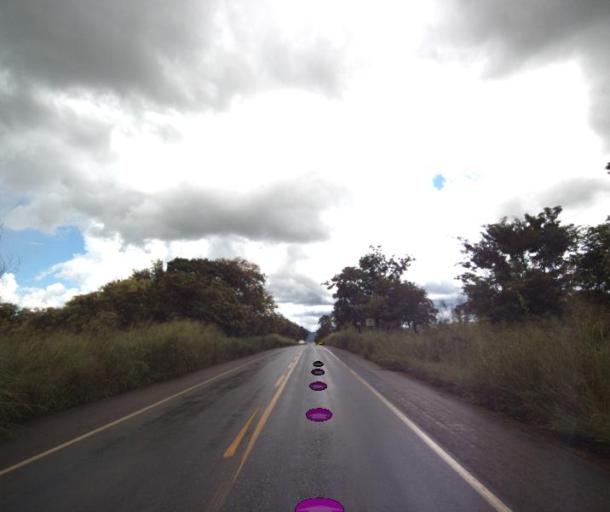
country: BR
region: Goias
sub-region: Pirenopolis
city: Pirenopolis
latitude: -16.0535
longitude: -49.0704
